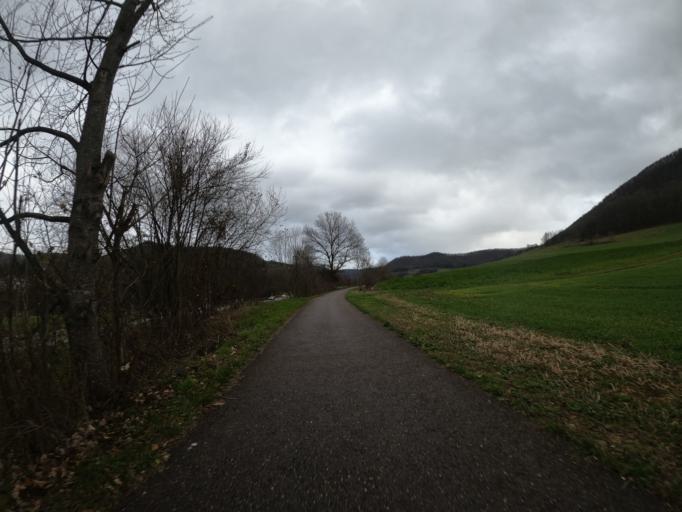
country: DE
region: Baden-Wuerttemberg
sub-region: Regierungsbezirk Stuttgart
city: Donzdorf
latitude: 48.6972
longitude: 9.8232
